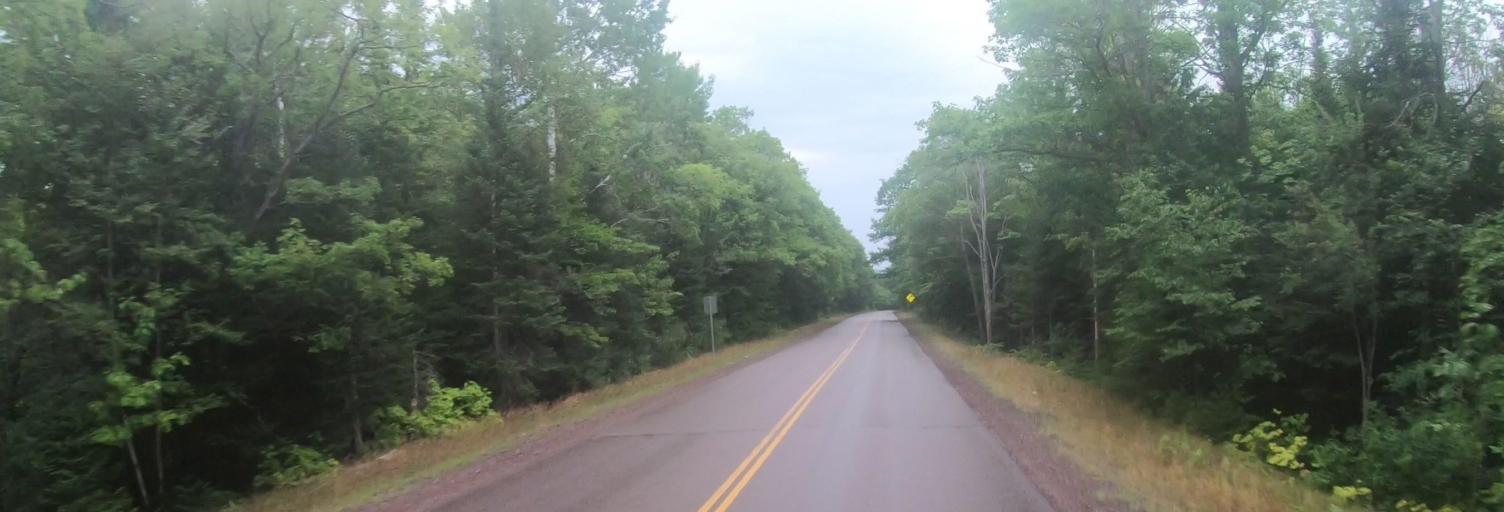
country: US
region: Michigan
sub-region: Keweenaw County
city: Eagle River
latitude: 47.2969
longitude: -88.3308
